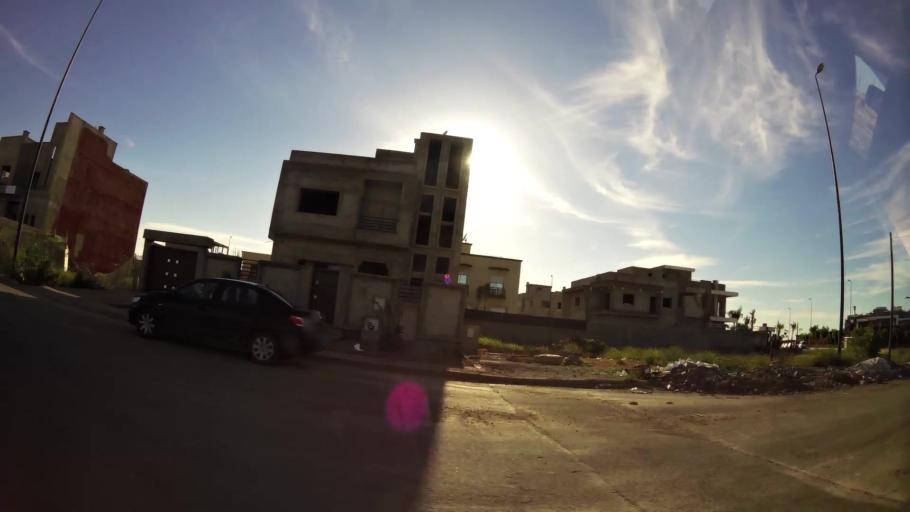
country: MA
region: Marrakech-Tensift-Al Haouz
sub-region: Marrakech
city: Marrakesh
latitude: 31.6730
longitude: -8.0731
